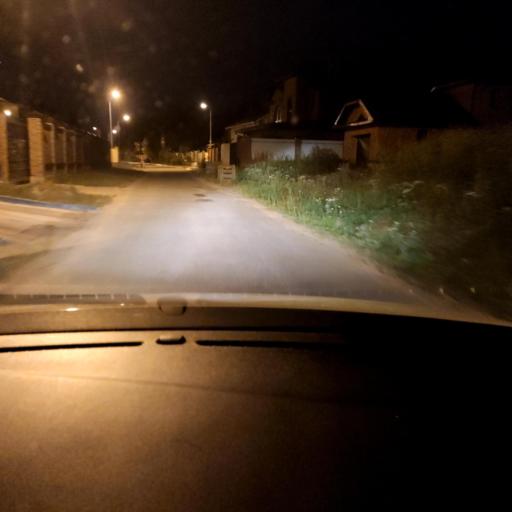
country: RU
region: Tatarstan
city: Osinovo
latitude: 55.8590
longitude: 48.7941
